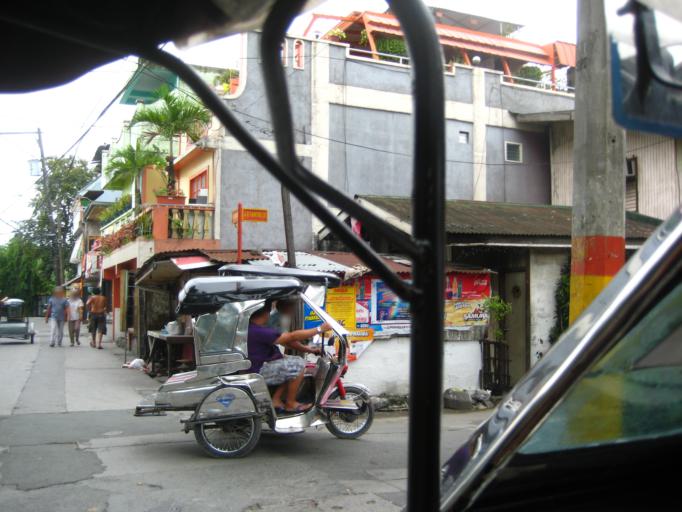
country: PH
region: Calabarzon
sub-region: Province of Rizal
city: Pateros
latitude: 14.5477
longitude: 121.0738
